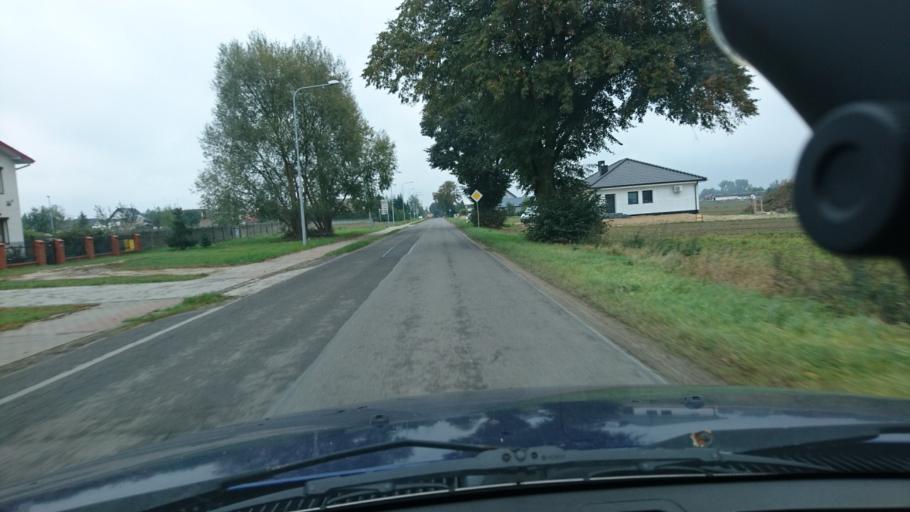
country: PL
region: Greater Poland Voivodeship
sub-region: Powiat ostrowski
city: Odolanow
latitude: 51.5764
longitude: 17.6519
